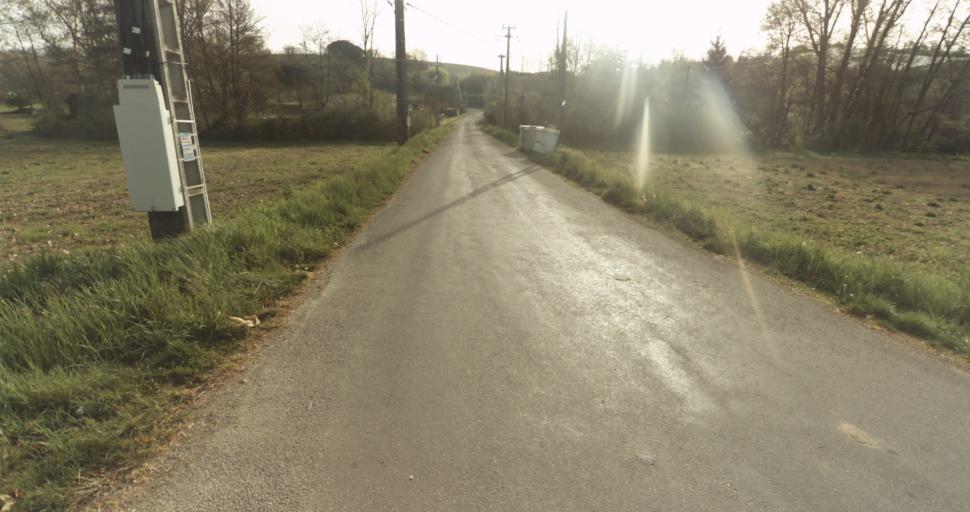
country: FR
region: Midi-Pyrenees
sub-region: Departement du Tarn-et-Garonne
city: Moissac
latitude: 44.1327
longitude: 1.1036
